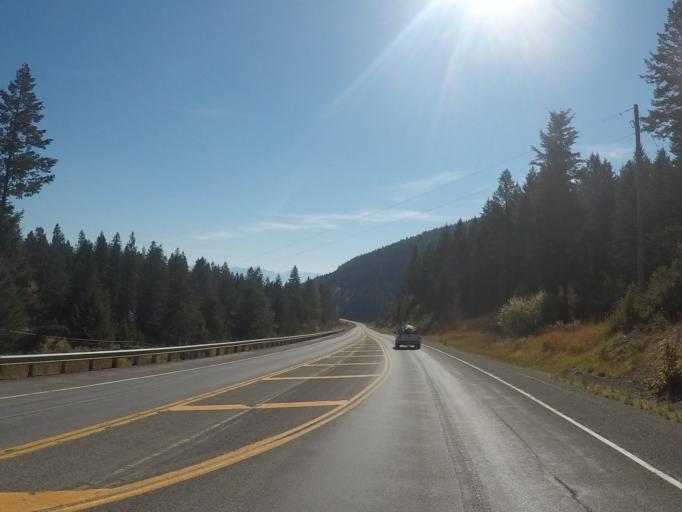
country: US
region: Montana
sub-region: Flathead County
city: Lakeside
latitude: 47.9762
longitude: -114.1989
